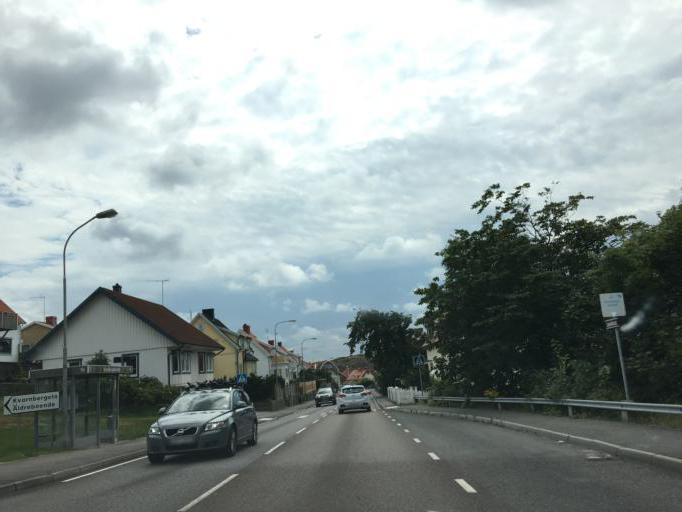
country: SE
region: Vaestra Goetaland
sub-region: Sotenas Kommun
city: Kungshamn
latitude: 58.3662
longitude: 11.2495
